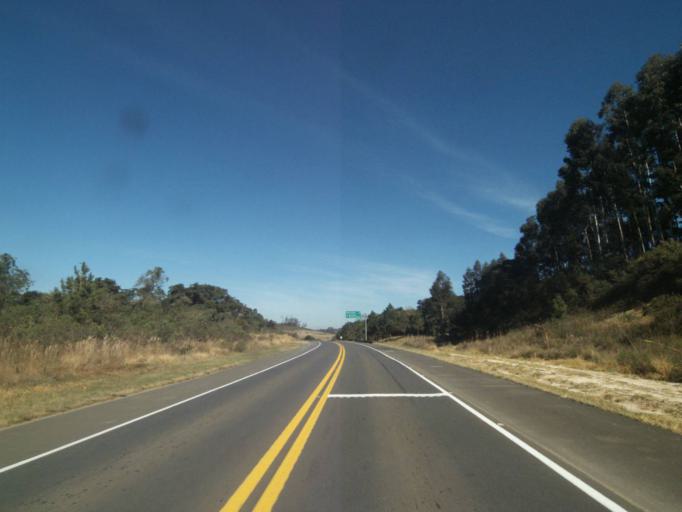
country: BR
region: Parana
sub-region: Tibagi
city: Tibagi
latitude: -24.8106
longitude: -50.4823
